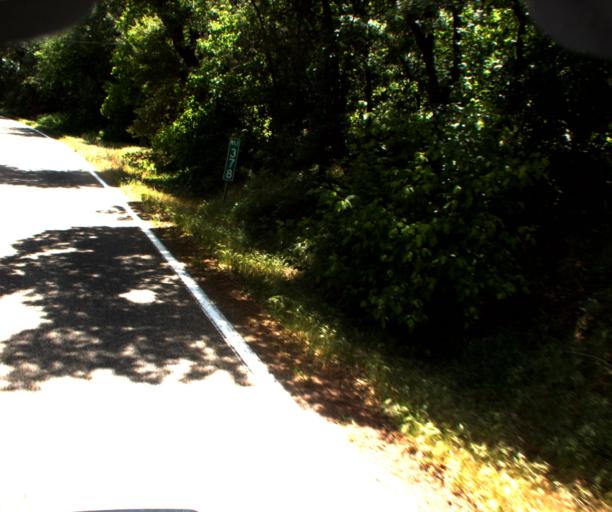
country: US
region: Arizona
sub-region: Coconino County
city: Sedona
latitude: 34.9083
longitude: -111.7288
